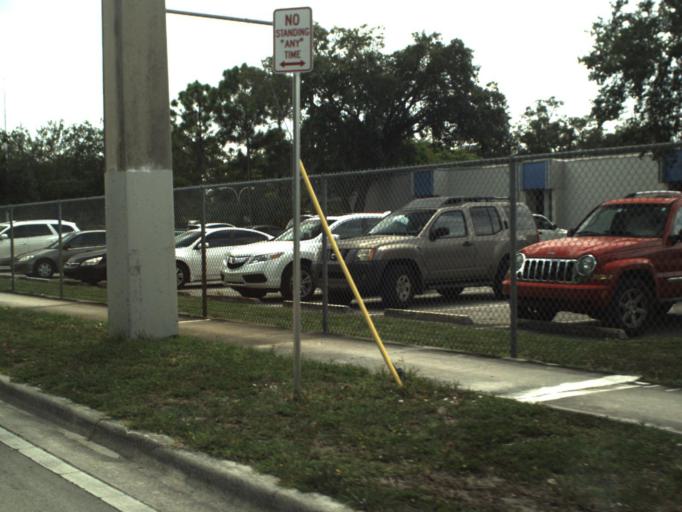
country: US
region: Florida
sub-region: Broward County
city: Davie
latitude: 26.0468
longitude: -80.1979
